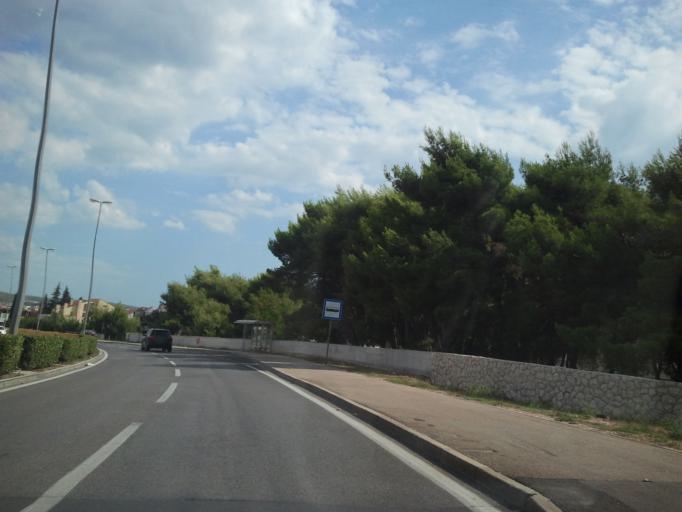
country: HR
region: Zadarska
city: Zadar
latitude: 44.1123
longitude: 15.2547
